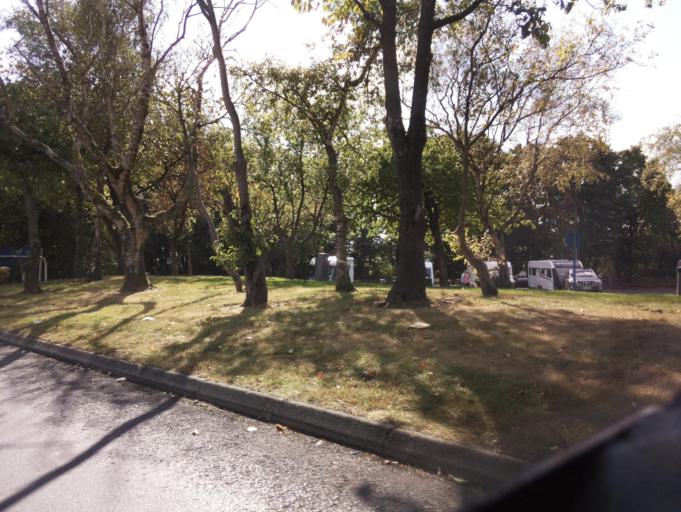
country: GB
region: England
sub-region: Lancashire
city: Bay Horse
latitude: 53.9613
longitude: -2.7615
